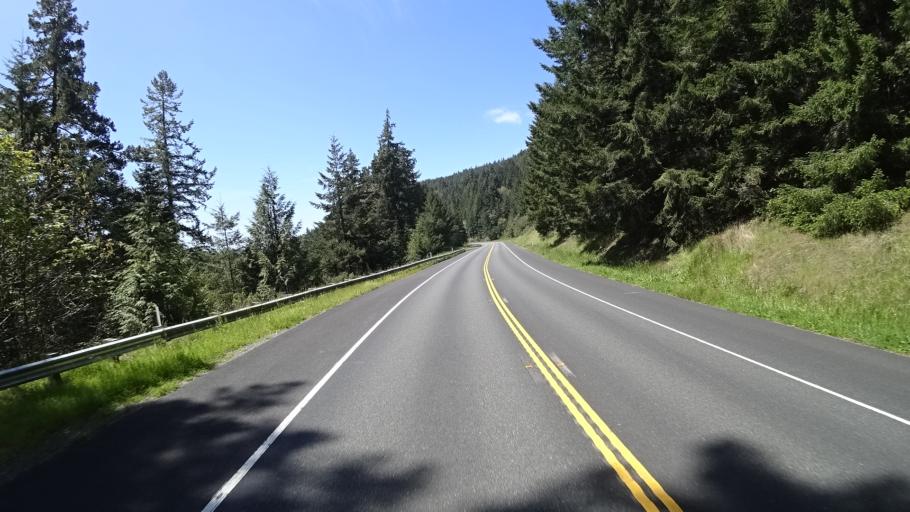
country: US
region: California
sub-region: Humboldt County
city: Blue Lake
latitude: 40.8976
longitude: -123.9280
